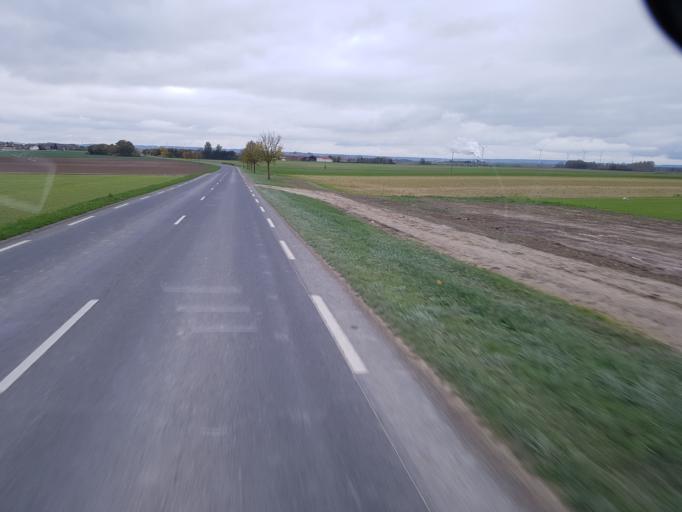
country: FR
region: Champagne-Ardenne
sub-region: Departement de la Marne
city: Saint-Just-Sauvage
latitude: 48.5857
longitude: 3.8380
